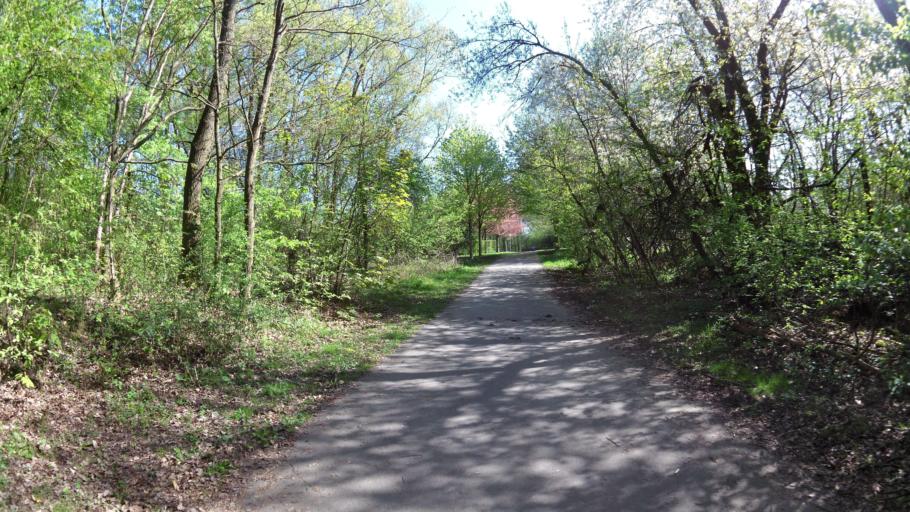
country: DE
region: North Rhine-Westphalia
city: Baesweiler
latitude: 50.9079
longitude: 6.1648
